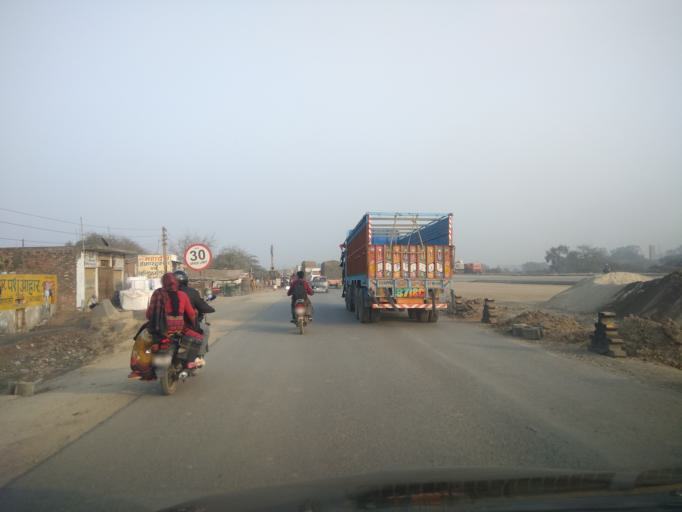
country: IN
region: Uttar Pradesh
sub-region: Varanasi
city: Ramnagar
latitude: 25.2522
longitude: 83.0643
